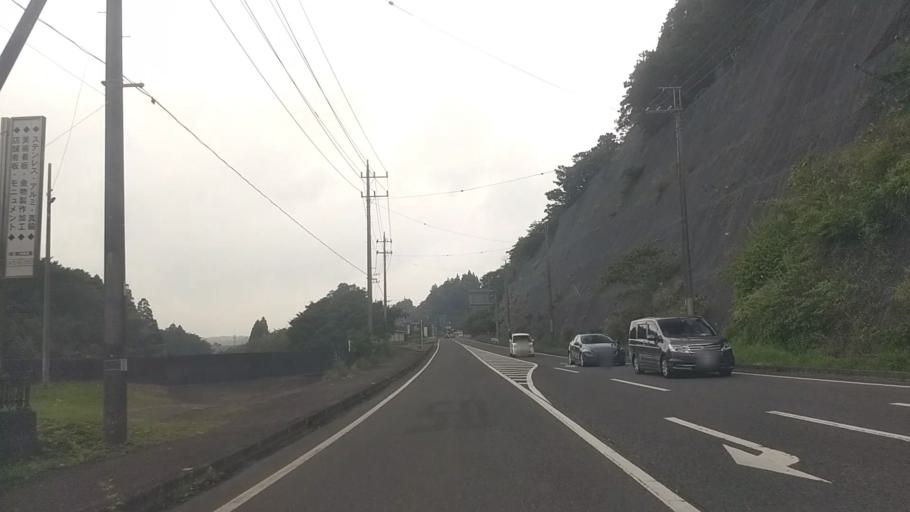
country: JP
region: Chiba
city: Ohara
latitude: 35.2718
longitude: 140.2549
